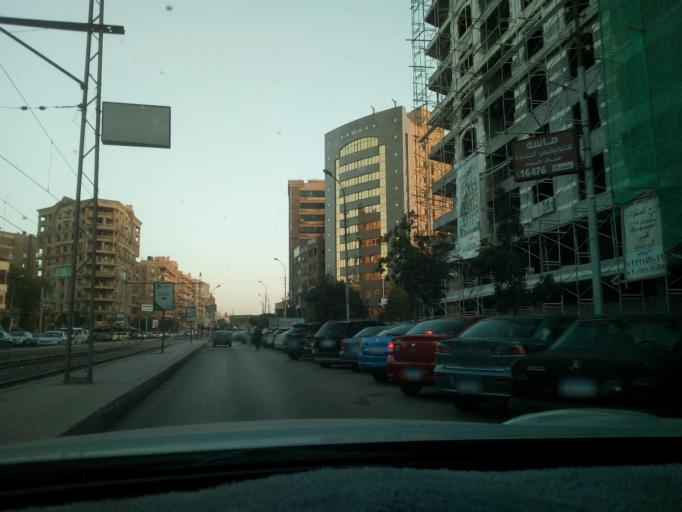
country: EG
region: Muhafazat al Qahirah
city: Cairo
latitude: 30.0883
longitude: 31.3448
